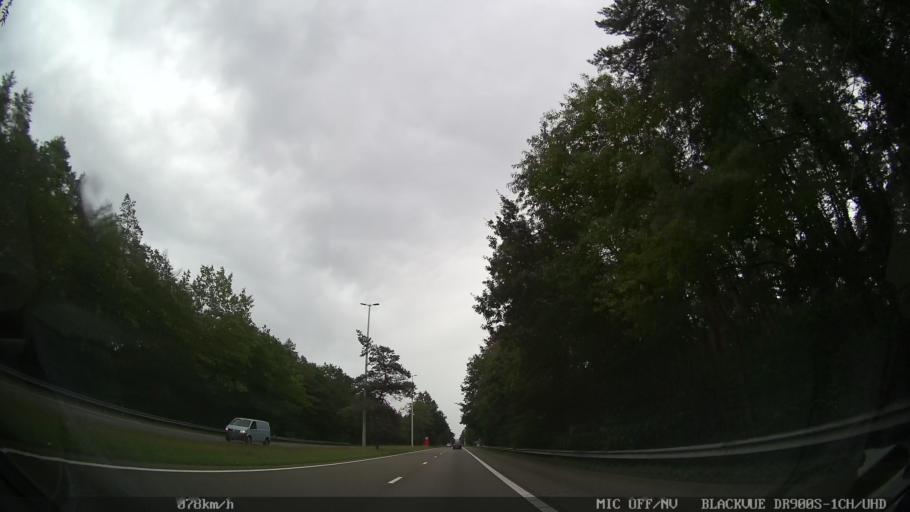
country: BE
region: Flanders
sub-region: Provincie Limburg
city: Genk
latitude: 50.9617
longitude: 5.5227
